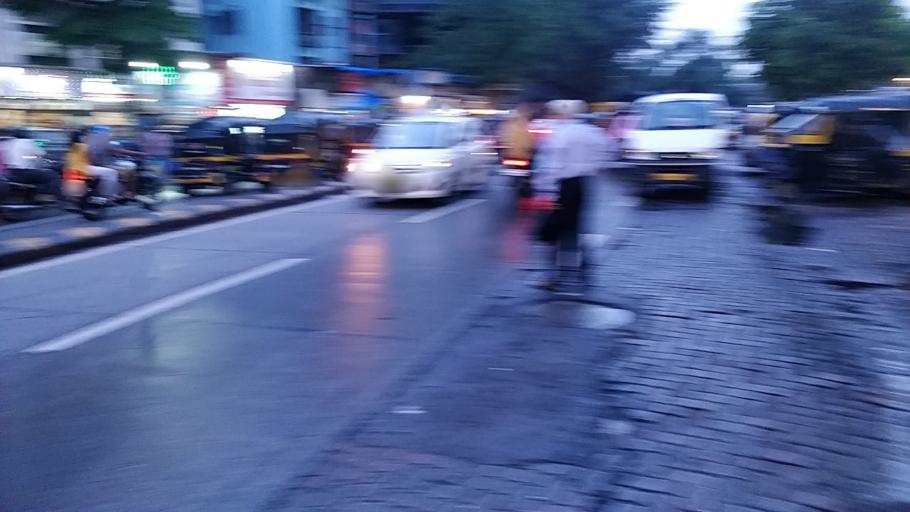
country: IN
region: Maharashtra
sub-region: Mumbai Suburban
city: Mumbai
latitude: 19.1130
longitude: 72.8480
